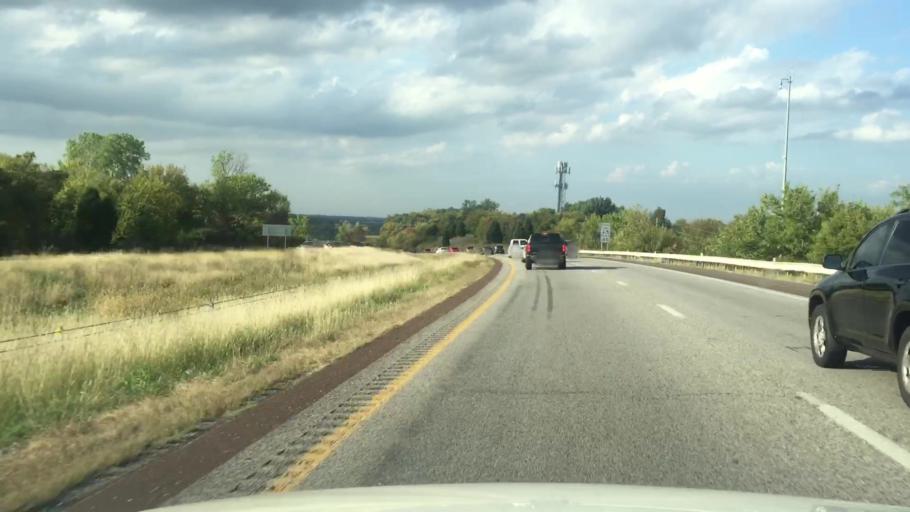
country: US
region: Missouri
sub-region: Jackson County
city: Blue Springs
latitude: 39.0132
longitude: -94.3565
